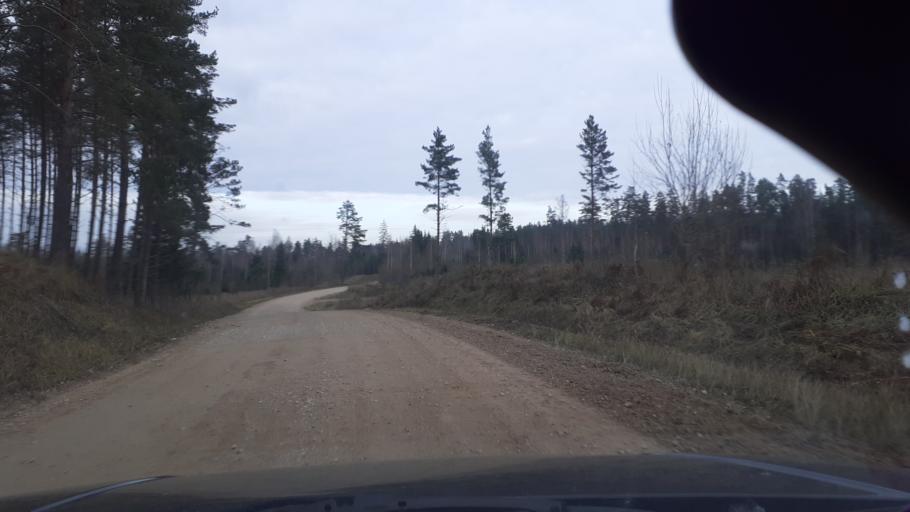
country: LV
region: Alsunga
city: Alsunga
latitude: 56.9815
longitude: 21.6687
